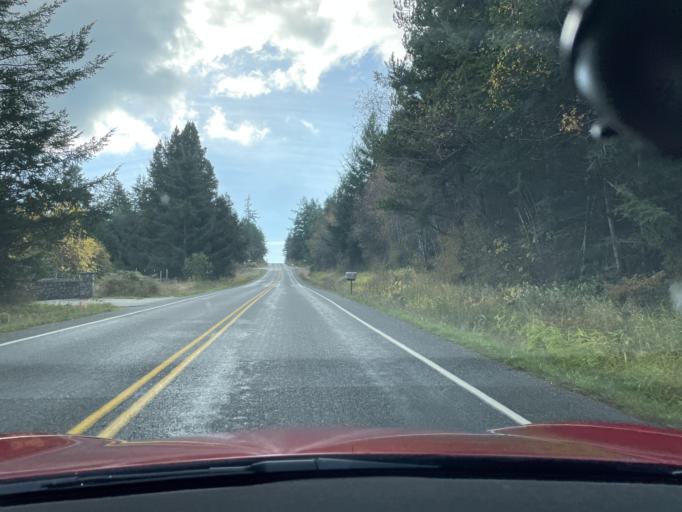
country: US
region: Washington
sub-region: San Juan County
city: Friday Harbor
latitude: 48.4872
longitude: -123.0314
